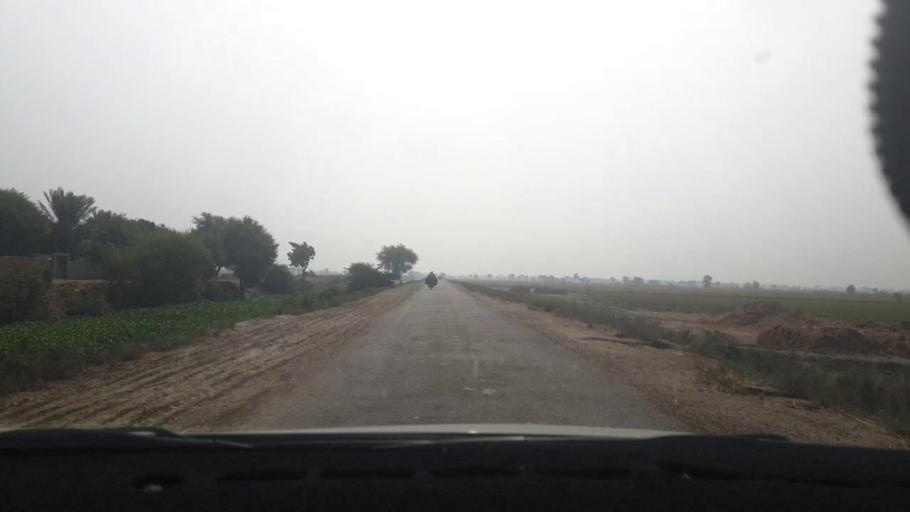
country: PK
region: Sindh
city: Tando Muhammad Khan
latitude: 25.0760
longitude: 68.5340
